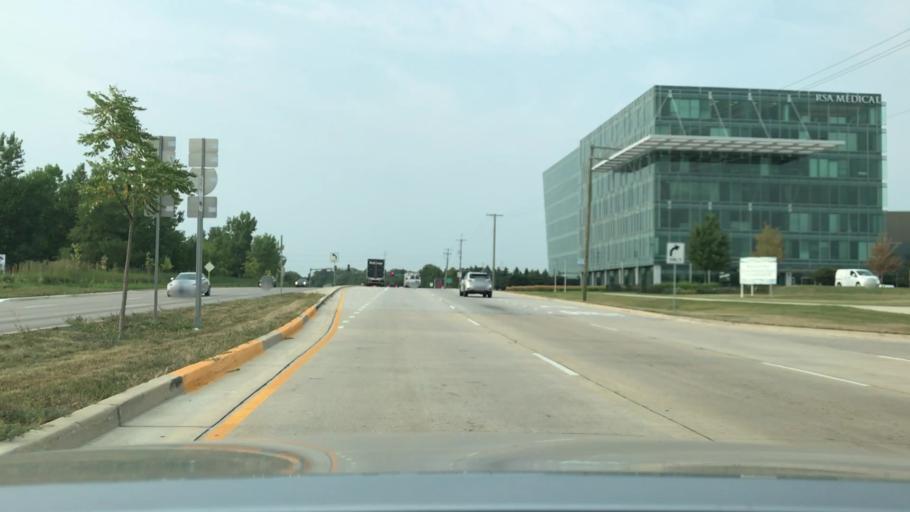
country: US
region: Illinois
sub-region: DuPage County
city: Warrenville
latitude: 41.8074
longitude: -88.2037
